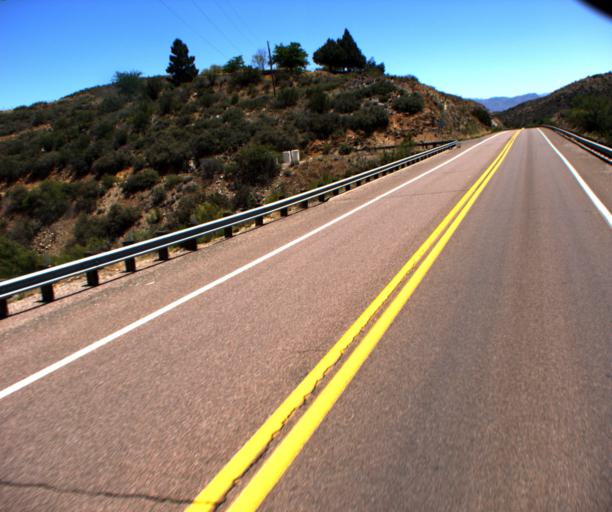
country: US
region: Arizona
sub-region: Yavapai County
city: Bagdad
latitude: 34.5640
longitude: -113.1692
